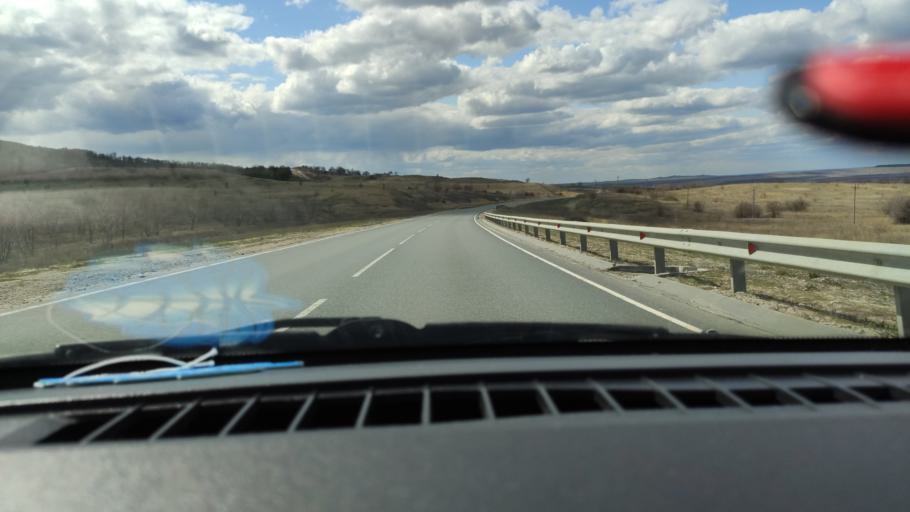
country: RU
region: Saratov
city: Alekseyevka
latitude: 52.3338
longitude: 47.9261
